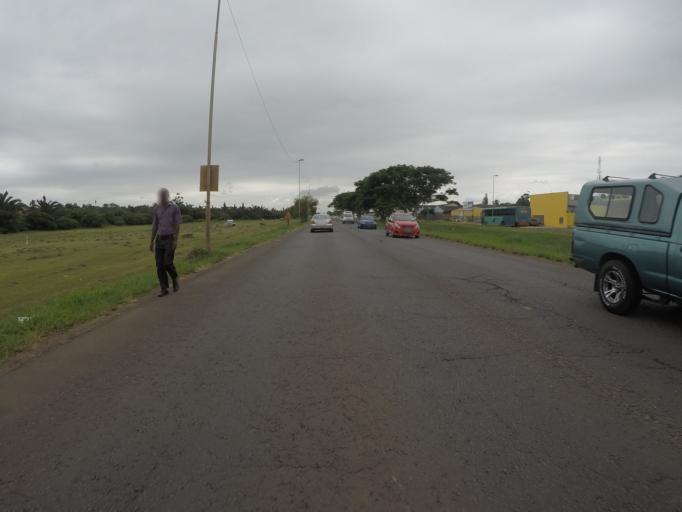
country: ZA
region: KwaZulu-Natal
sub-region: uThungulu District Municipality
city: Empangeni
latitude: -28.7704
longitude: 31.9030
